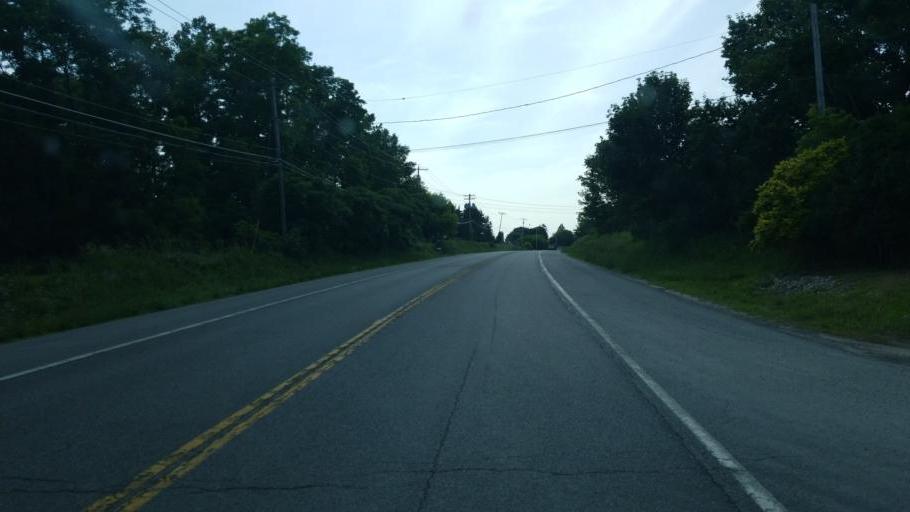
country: US
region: New York
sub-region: Ontario County
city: Holcomb
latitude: 42.9019
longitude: -77.4889
